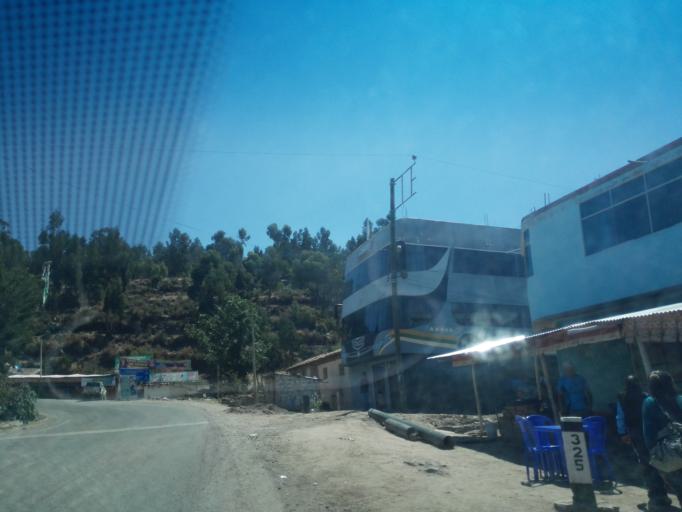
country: PE
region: Ayacucho
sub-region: Provincia de Huamanga
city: Ayacucho
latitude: -13.1648
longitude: -74.2494
